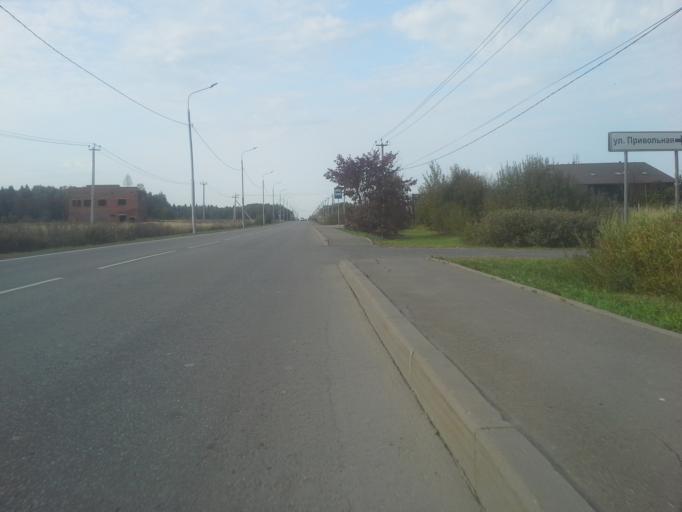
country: RU
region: Moskovskaya
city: Selyatino
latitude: 55.4331
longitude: 36.9594
